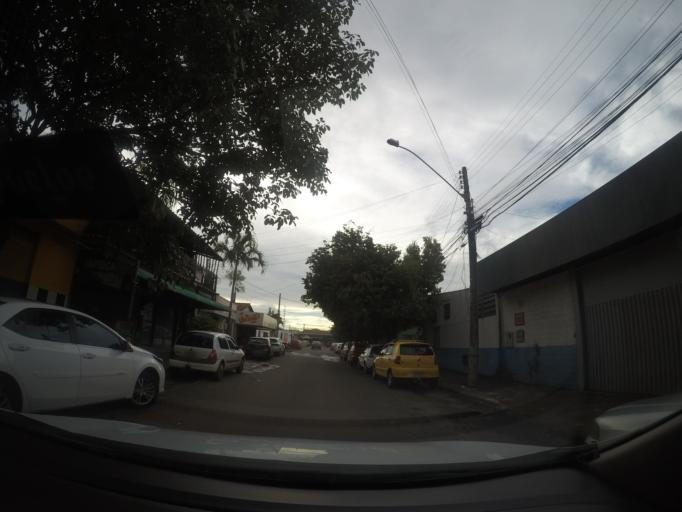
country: BR
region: Goias
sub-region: Goiania
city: Goiania
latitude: -16.6744
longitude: -49.2906
